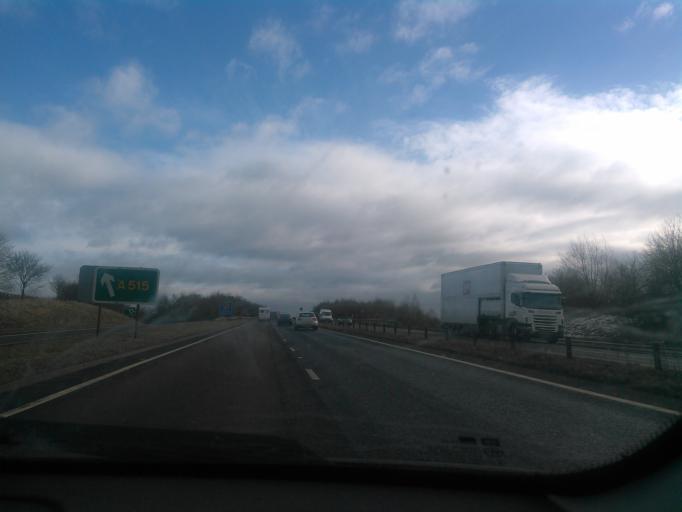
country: GB
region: England
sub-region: Staffordshire
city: Uttoxeter
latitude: 52.8946
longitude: -1.7794
